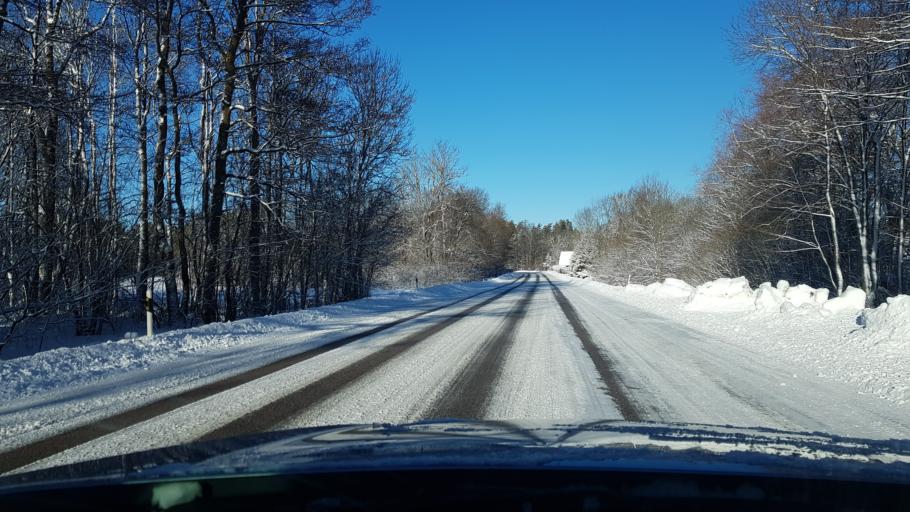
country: EE
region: Hiiumaa
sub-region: Kaerdla linn
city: Kardla
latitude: 58.9195
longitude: 22.7944
